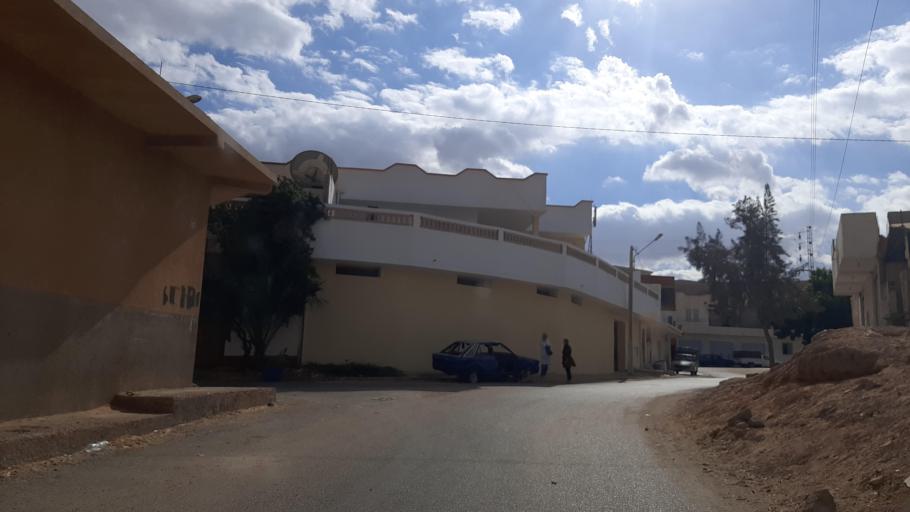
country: TN
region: Tataouine
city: Tataouine
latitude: 32.9218
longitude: 10.4629
